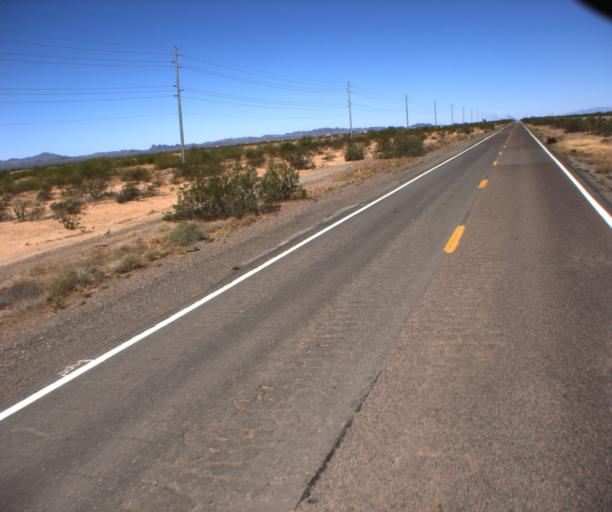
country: US
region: Arizona
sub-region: La Paz County
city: Salome
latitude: 33.8420
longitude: -113.8918
